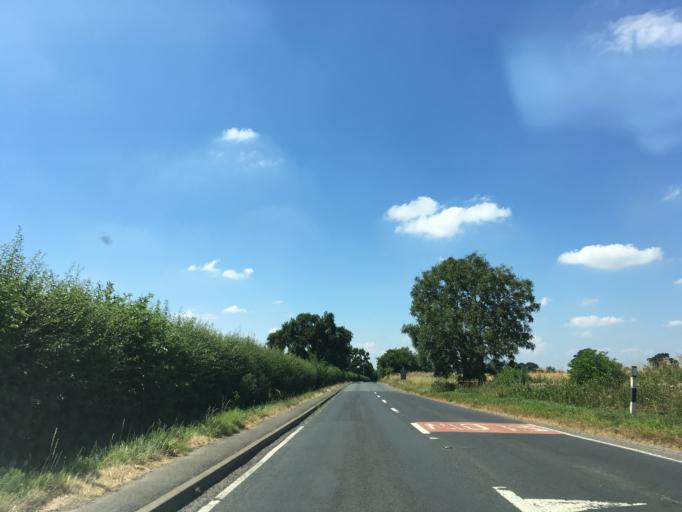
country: GB
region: England
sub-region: Gloucestershire
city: Tetbury
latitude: 51.6282
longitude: -2.1383
